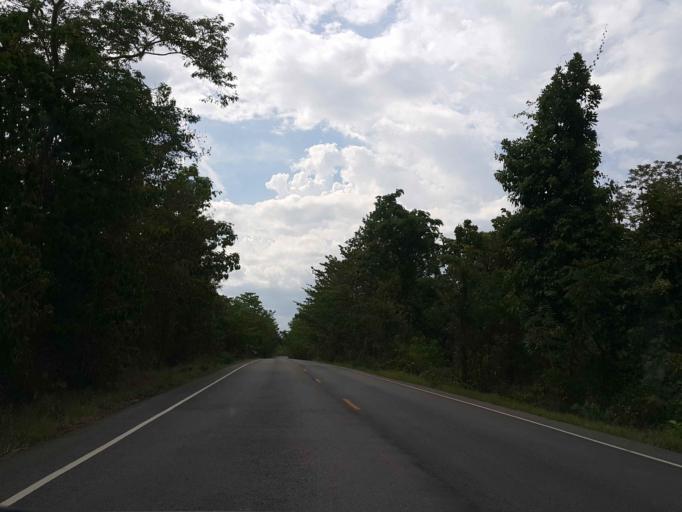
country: TH
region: Sukhothai
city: Thung Saliam
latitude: 17.4285
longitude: 99.3767
